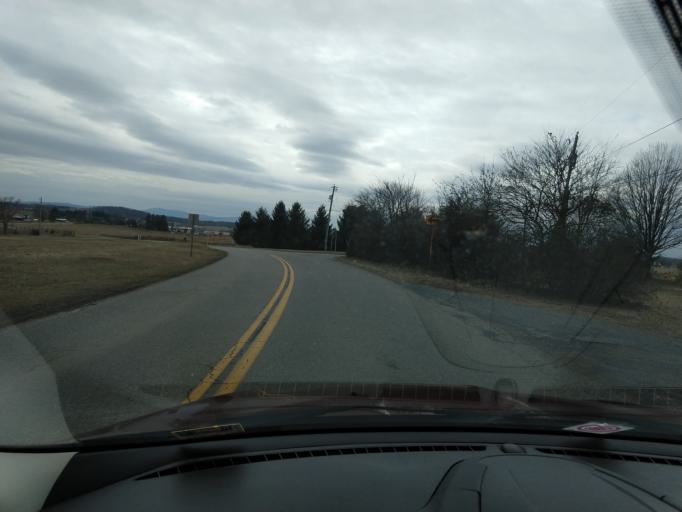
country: US
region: Virginia
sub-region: Augusta County
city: Crimora
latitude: 38.1743
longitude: -78.9155
